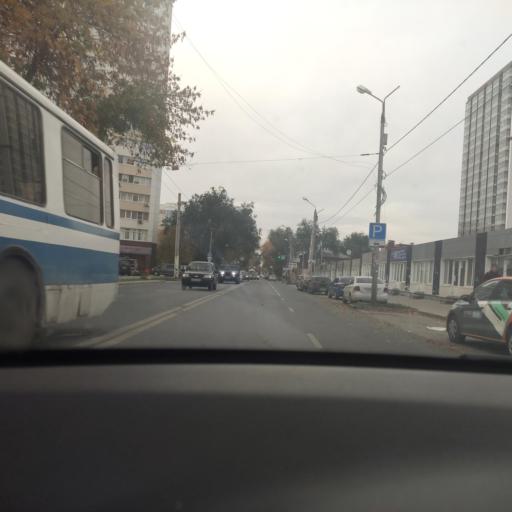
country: RU
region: Samara
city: Samara
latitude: 53.1964
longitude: 50.1239
